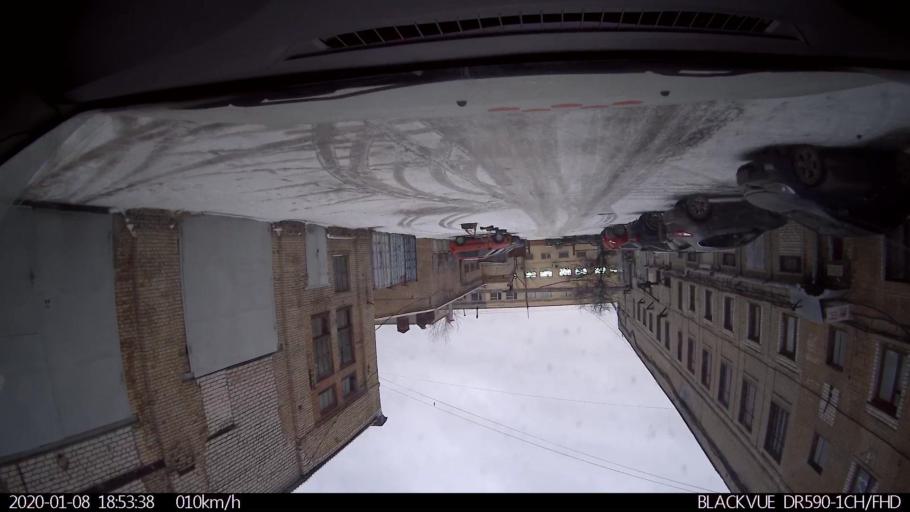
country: RU
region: Nizjnij Novgorod
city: Nizhniy Novgorod
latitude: 56.2710
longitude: 43.9428
